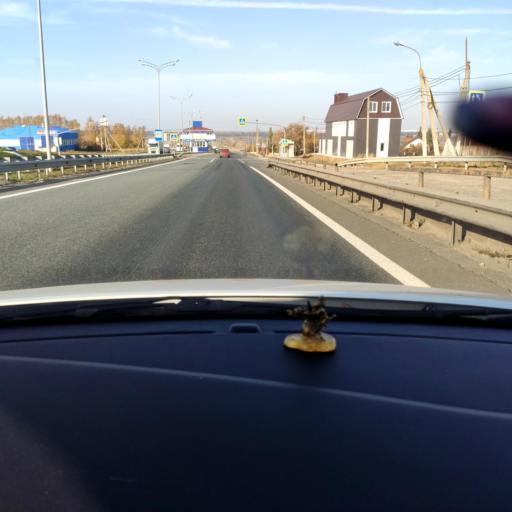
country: RU
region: Tatarstan
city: Osinovo
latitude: 55.7775
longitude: 48.8401
